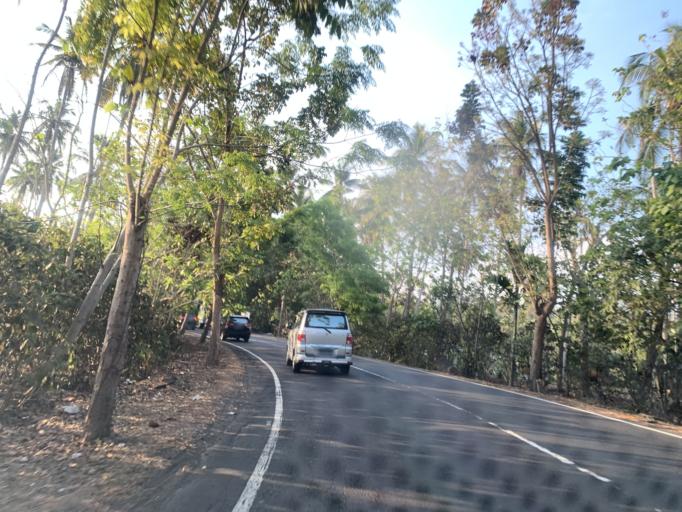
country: ID
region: Bali
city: Angkahgede
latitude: -8.4834
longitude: 114.9444
